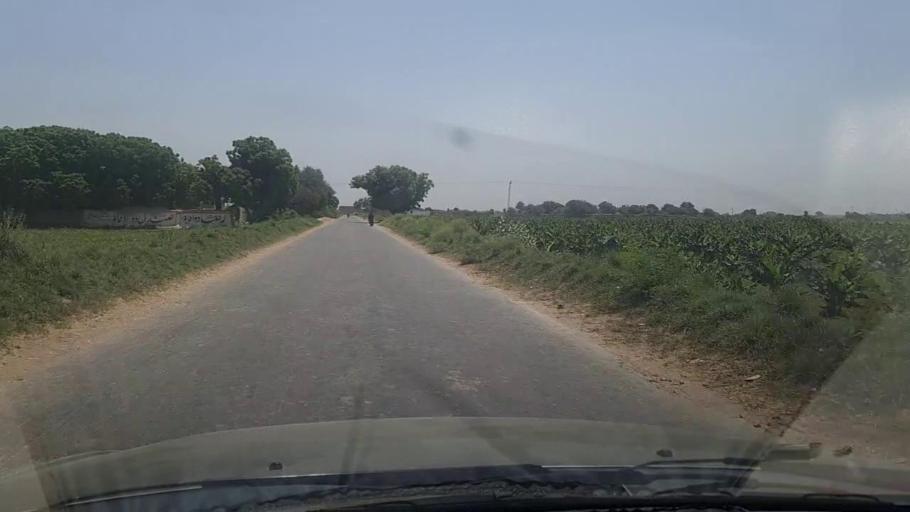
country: PK
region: Sindh
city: Chambar
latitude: 25.2673
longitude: 68.6407
